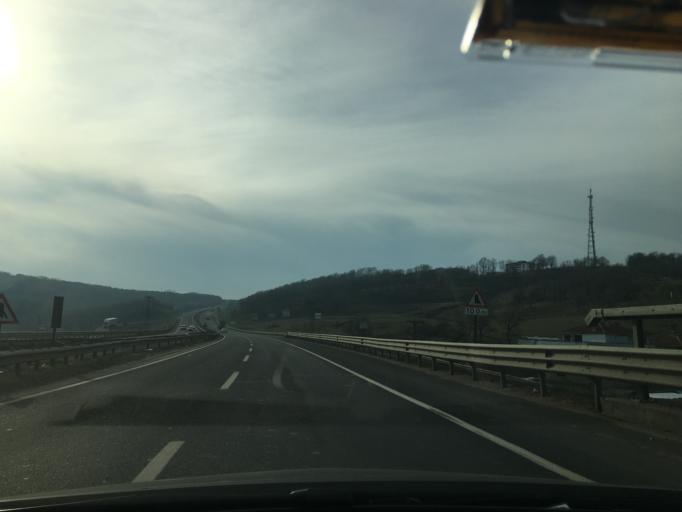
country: TR
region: Tekirdag
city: Cerkezkoey
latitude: 41.2754
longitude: 28.0264
